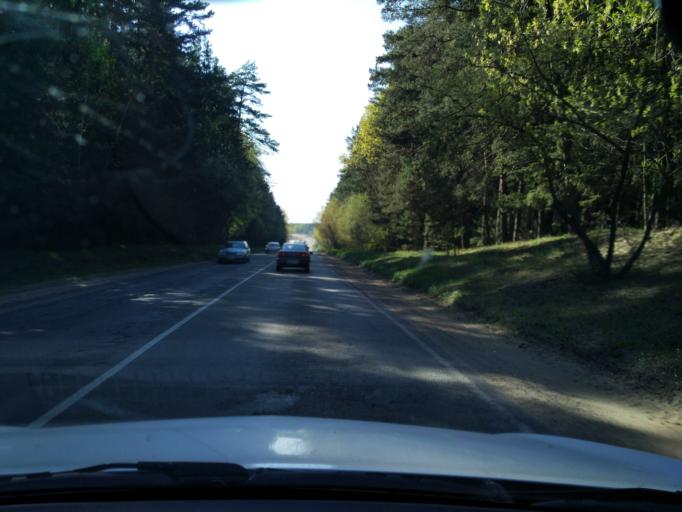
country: BY
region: Minsk
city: Borovlyany
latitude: 53.9629
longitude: 27.6799
